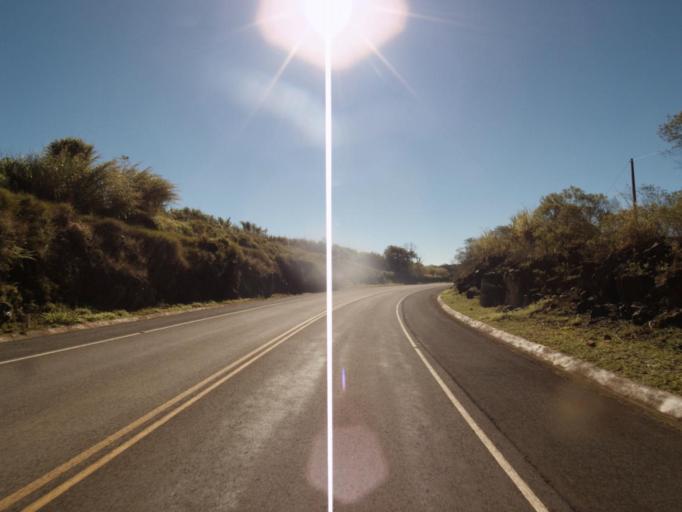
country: AR
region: Misiones
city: Bernardo de Irigoyen
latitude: -26.6686
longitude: -53.5998
